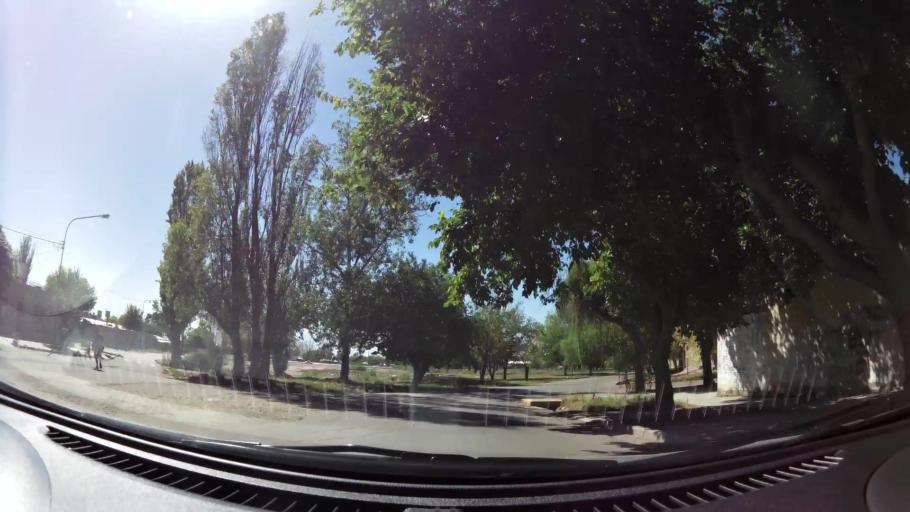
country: AR
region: Mendoza
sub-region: Departamento de Godoy Cruz
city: Godoy Cruz
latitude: -32.9598
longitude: -68.8400
